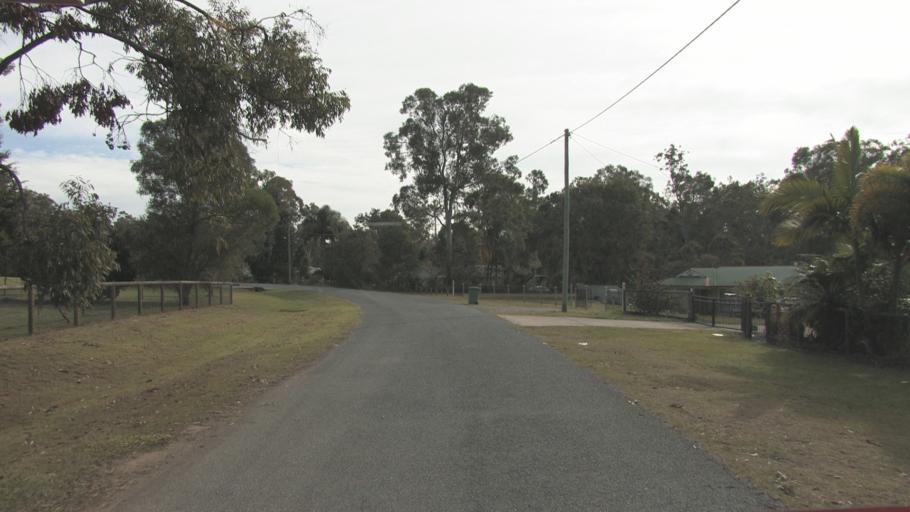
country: AU
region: Queensland
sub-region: Logan
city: Park Ridge South
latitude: -27.7383
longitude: 153.0370
